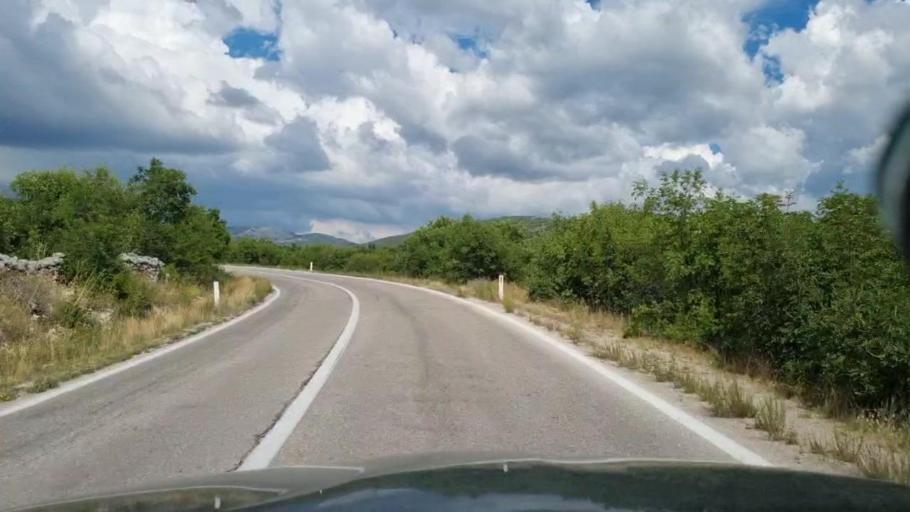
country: BA
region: Federation of Bosnia and Herzegovina
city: Blagaj
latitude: 43.2492
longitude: 17.9847
